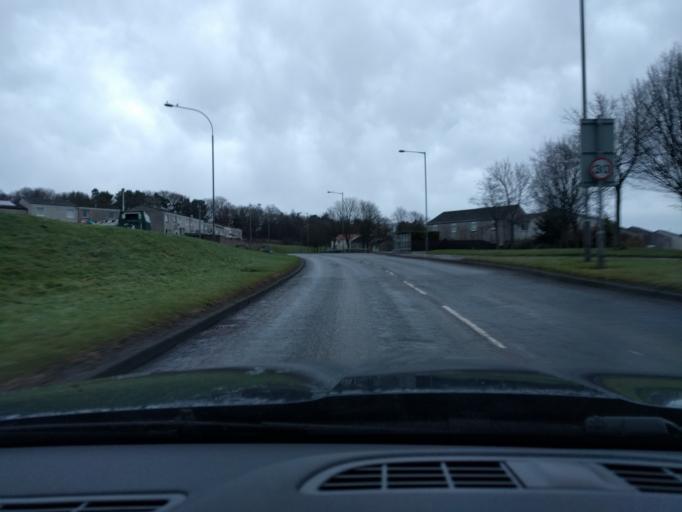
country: GB
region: Scotland
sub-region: Falkirk
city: Falkirk
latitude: 55.9865
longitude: -3.7800
